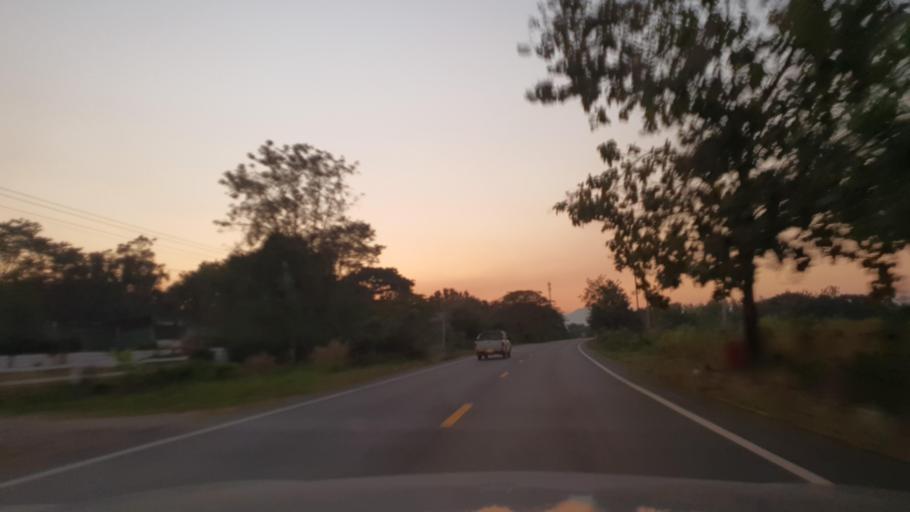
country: TH
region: Phayao
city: Dok Kham Tai
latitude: 19.1477
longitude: 100.0077
